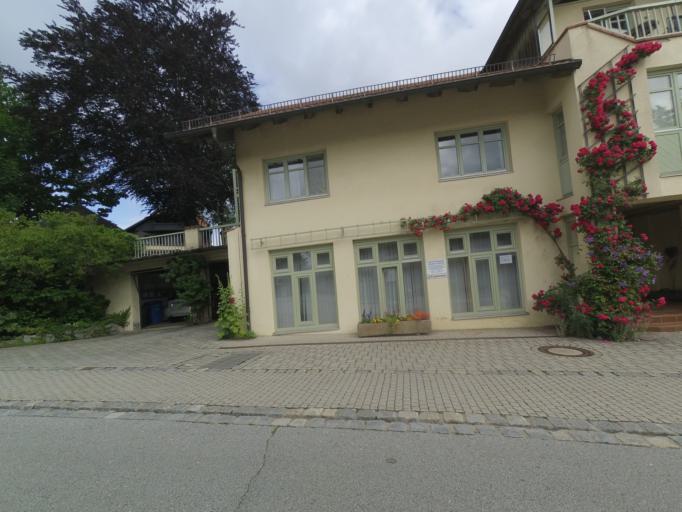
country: DE
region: Bavaria
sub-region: Lower Bavaria
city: Mitterfels
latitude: 48.9731
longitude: 12.6774
